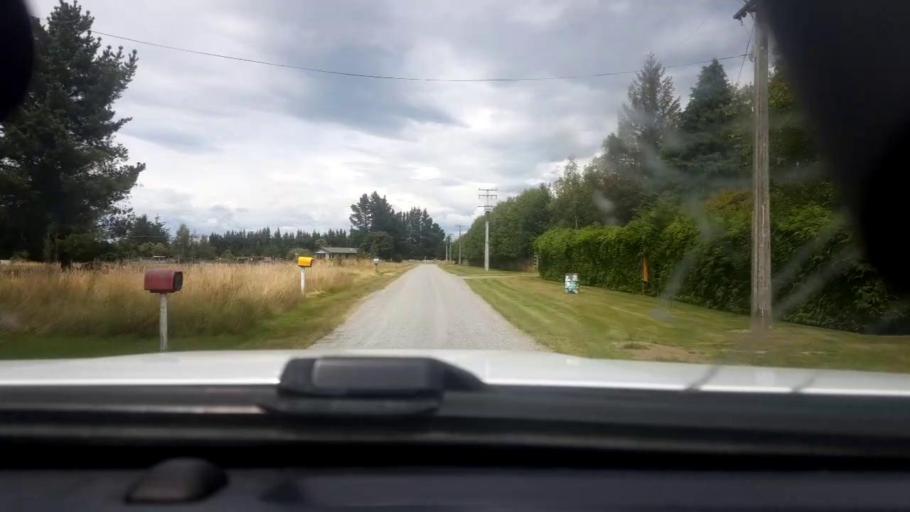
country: NZ
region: Canterbury
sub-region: Timaru District
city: Pleasant Point
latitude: -44.1428
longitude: 171.2892
